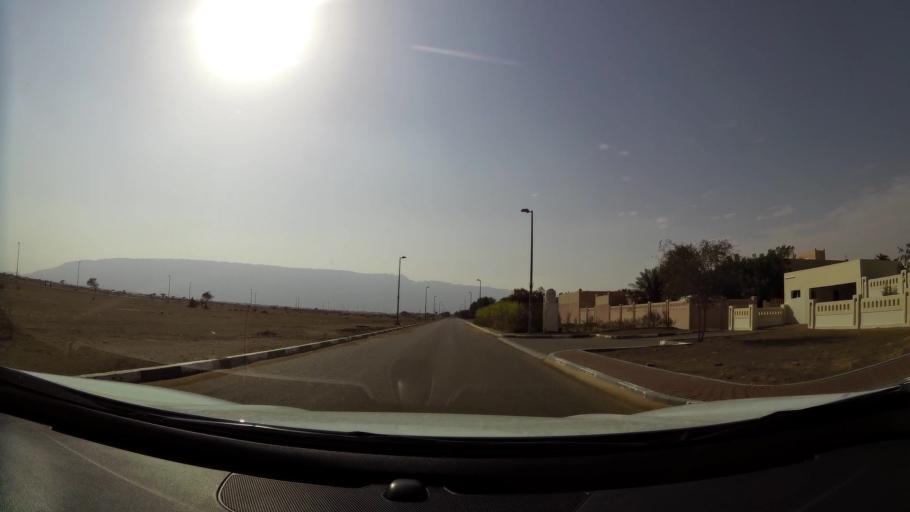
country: AE
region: Abu Dhabi
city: Al Ain
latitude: 24.0699
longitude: 55.8721
